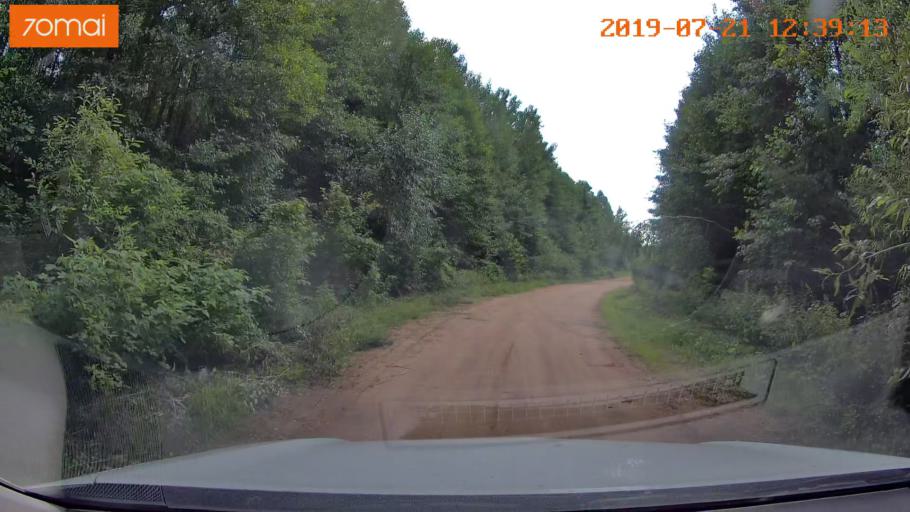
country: BY
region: Grodnenskaya
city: Lyubcha
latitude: 53.8571
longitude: 26.0161
